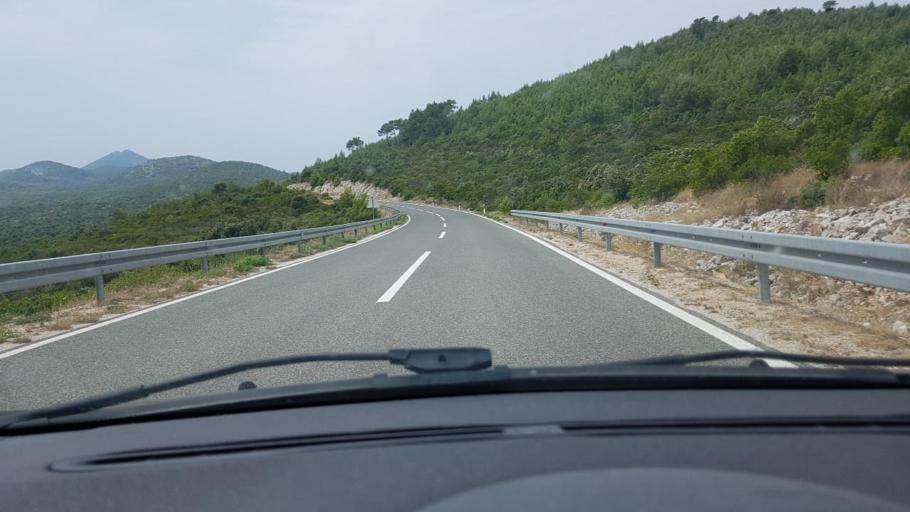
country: HR
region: Dubrovacko-Neretvanska
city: Smokvica
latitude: 42.9558
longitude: 16.9338
